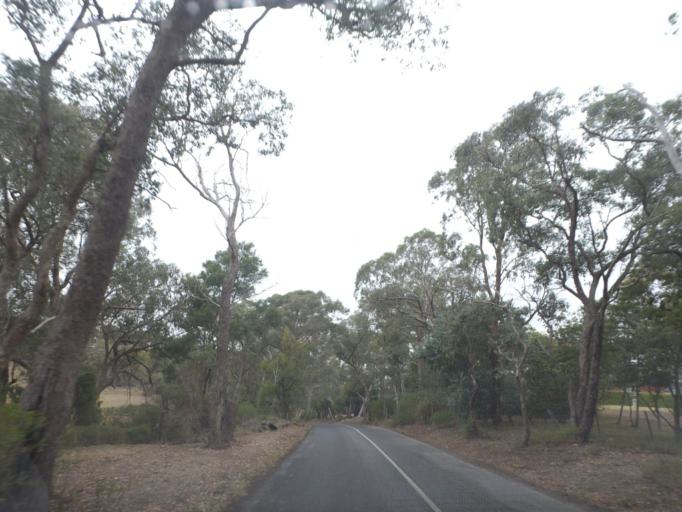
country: AU
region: Victoria
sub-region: Nillumbik
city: North Warrandyte
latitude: -37.6968
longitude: 145.2494
